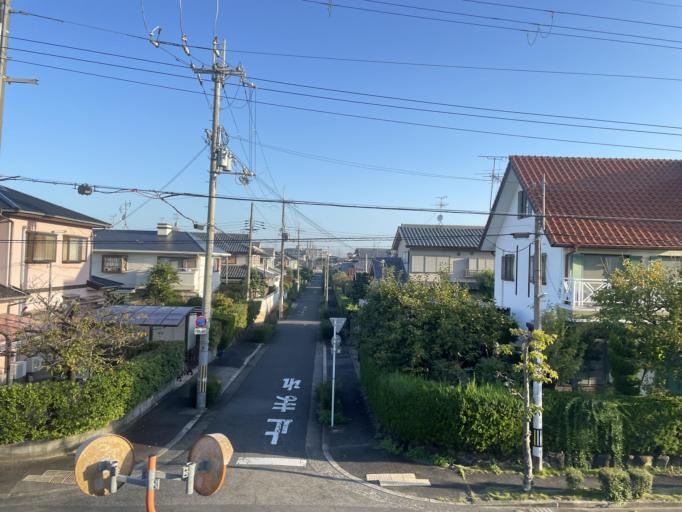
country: JP
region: Osaka
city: Kashihara
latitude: 34.5718
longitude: 135.5879
